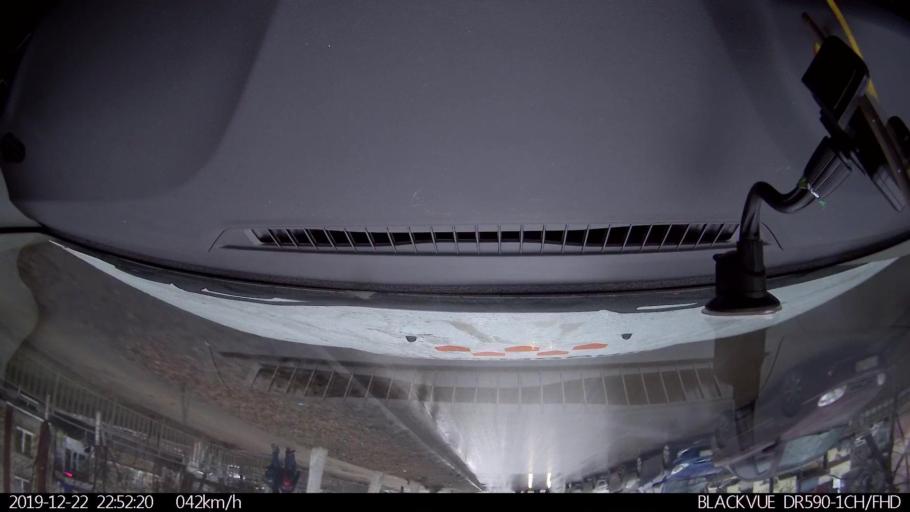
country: RU
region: Nizjnij Novgorod
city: Gorbatovka
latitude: 56.2429
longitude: 43.8598
